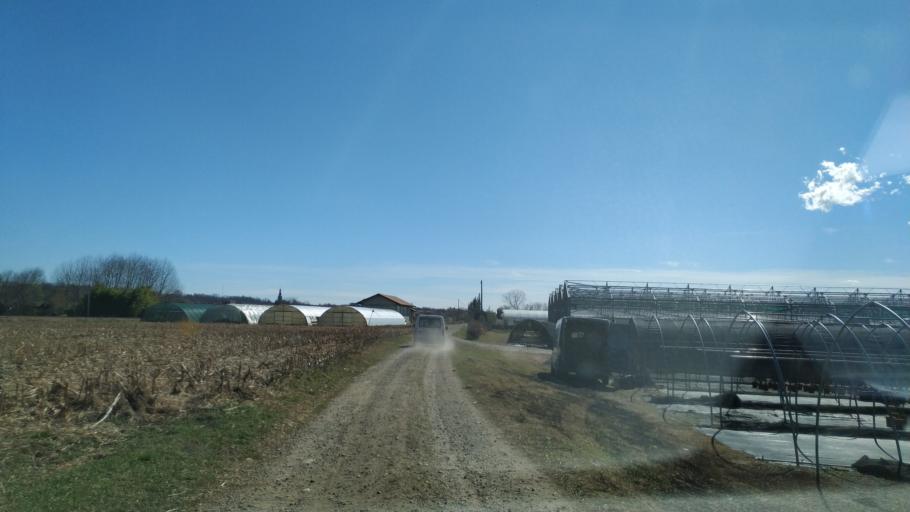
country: IT
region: Piedmont
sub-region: Provincia di Novara
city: Ghemme
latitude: 45.6030
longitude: 8.4061
